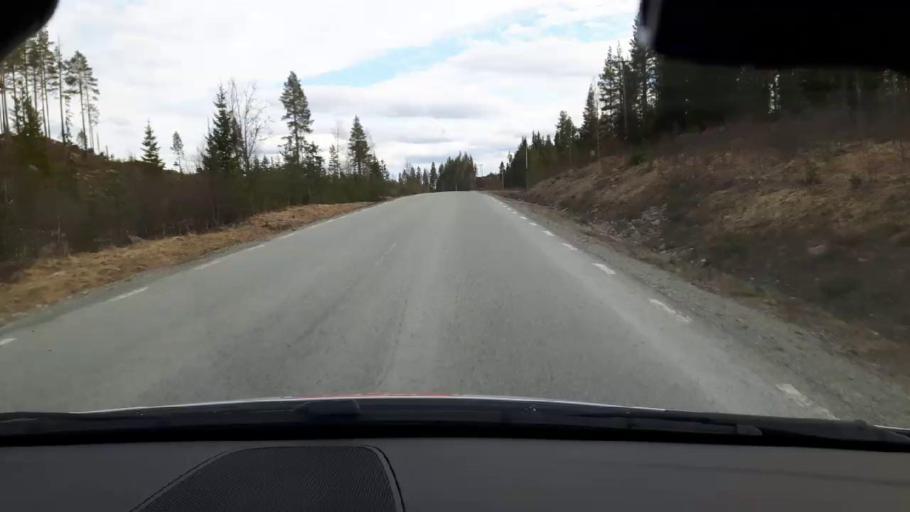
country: SE
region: Jaemtland
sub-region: Bergs Kommun
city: Hoverberg
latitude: 62.6978
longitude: 14.6245
